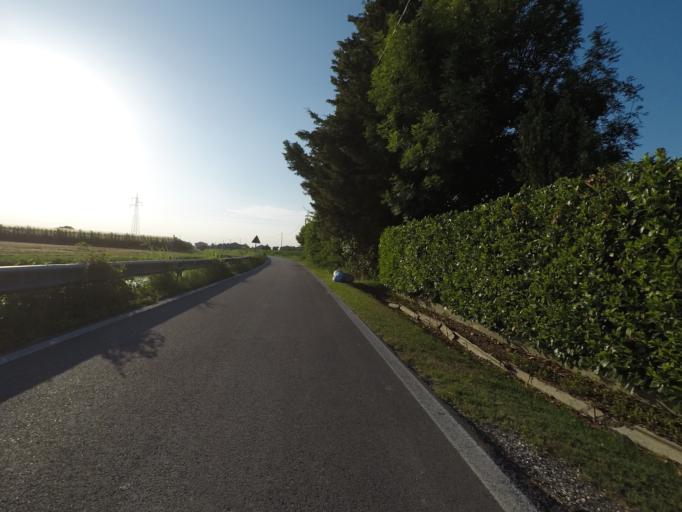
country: IT
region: Veneto
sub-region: Provincia di Rovigo
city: Villamarzana
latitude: 45.0315
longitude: 11.6765
